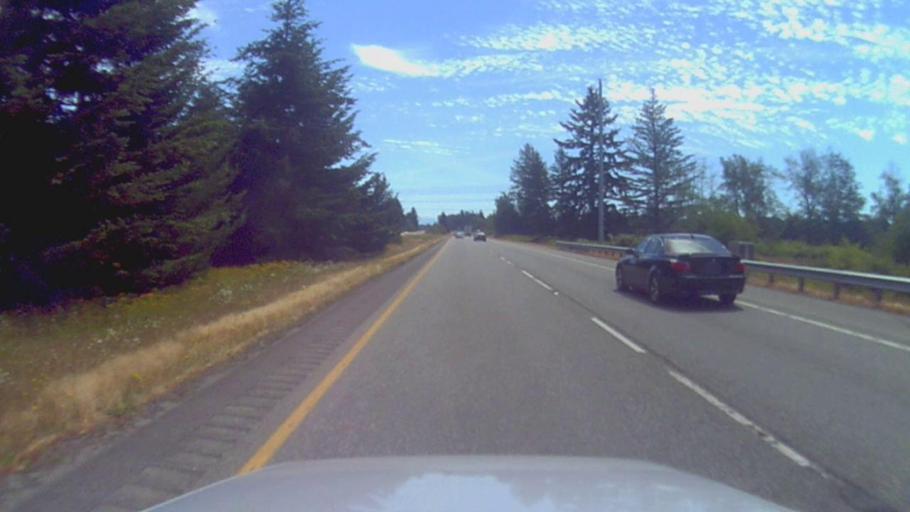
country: US
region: Washington
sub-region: Whatcom County
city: Ferndale
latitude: 48.9095
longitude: -122.6247
